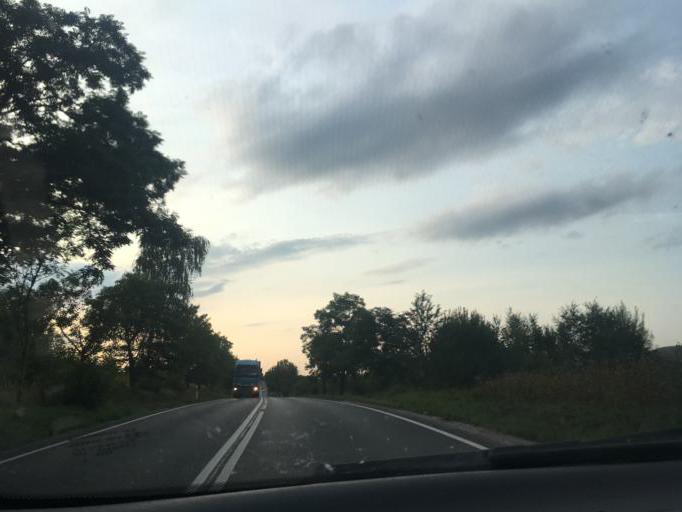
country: PL
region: Lower Silesian Voivodeship
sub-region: Powiat klodzki
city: Nowa Ruda
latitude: 50.5568
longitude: 16.5449
